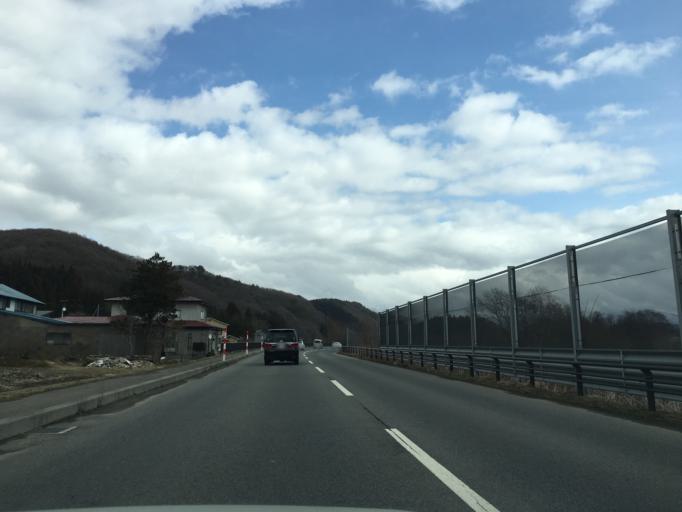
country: JP
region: Akita
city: Hanawa
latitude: 40.2335
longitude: 140.6977
